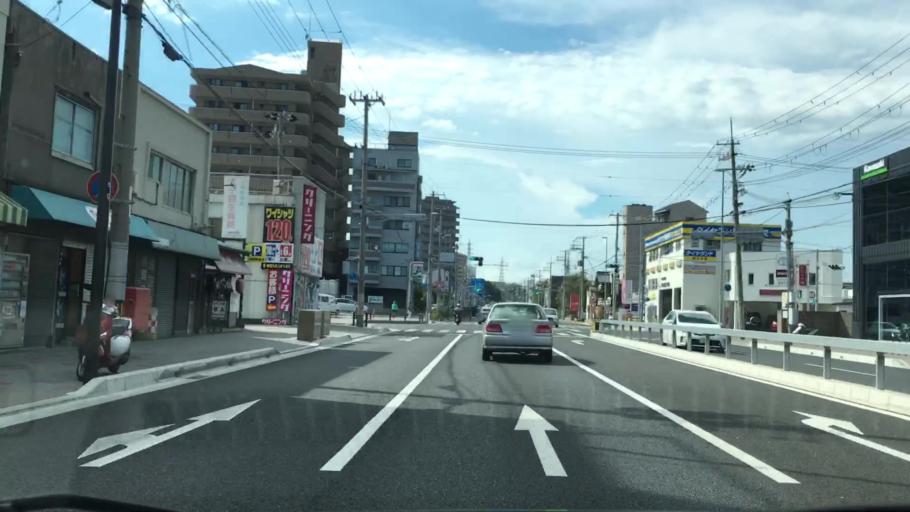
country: JP
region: Hyogo
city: Akashi
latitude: 34.6515
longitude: 134.9793
